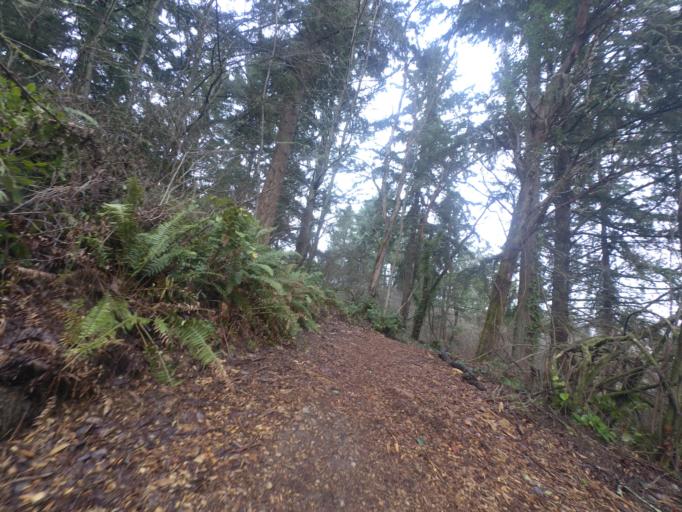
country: US
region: Washington
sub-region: Pierce County
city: University Place
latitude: 47.2252
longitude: -122.5486
